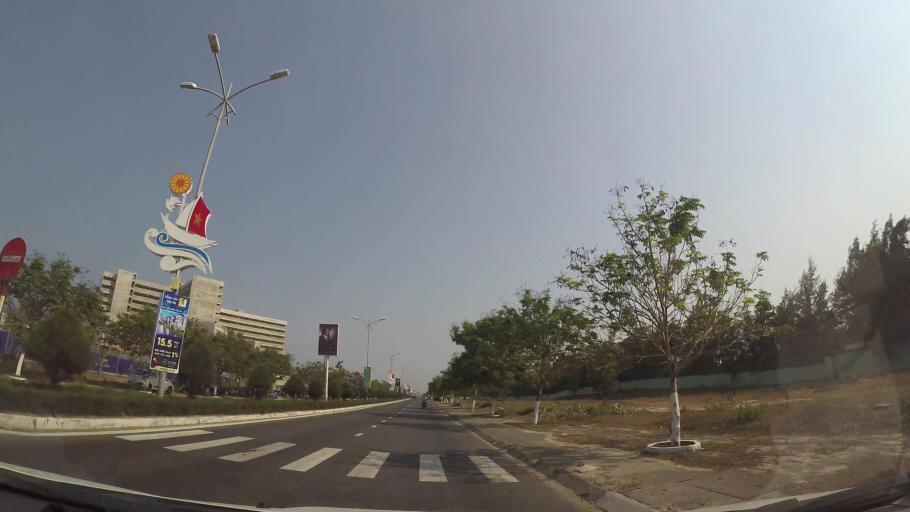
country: VN
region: Da Nang
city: Ngu Hanh Son
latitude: 15.9639
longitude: 108.2870
